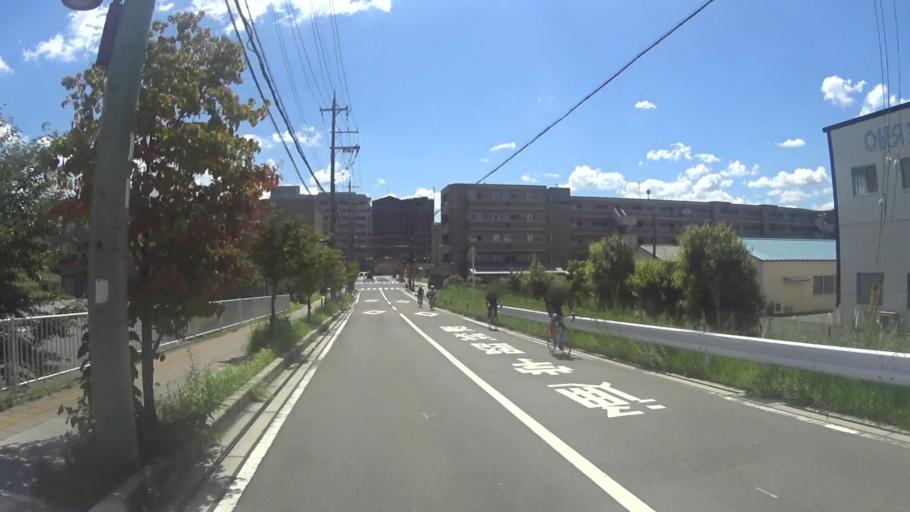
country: JP
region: Nara
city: Nara-shi
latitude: 34.7384
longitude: 135.8240
